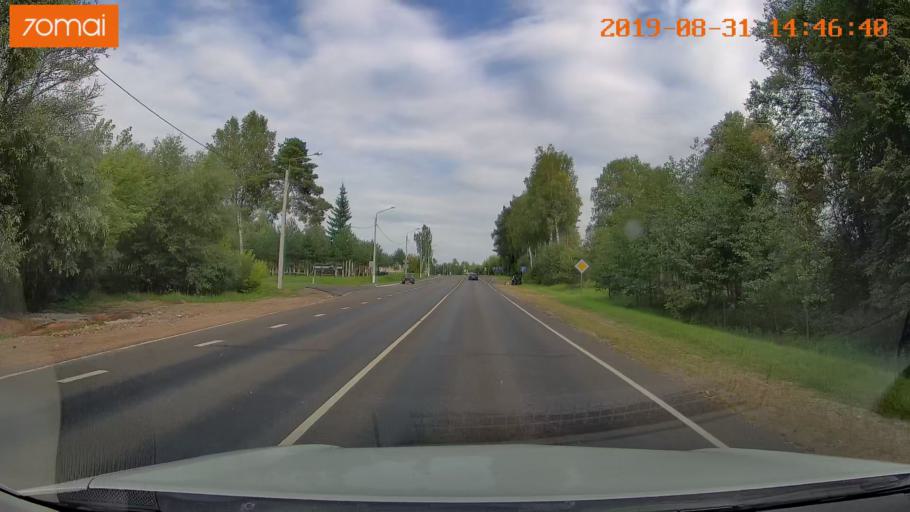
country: RU
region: Kaluga
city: Betlitsa
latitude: 54.2355
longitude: 33.7142
